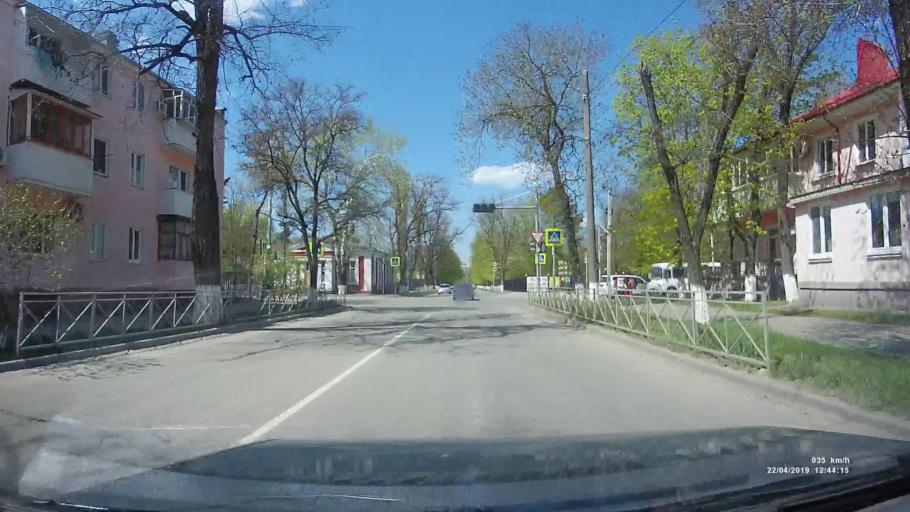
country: RU
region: Rostov
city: Azov
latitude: 47.1036
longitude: 39.4184
